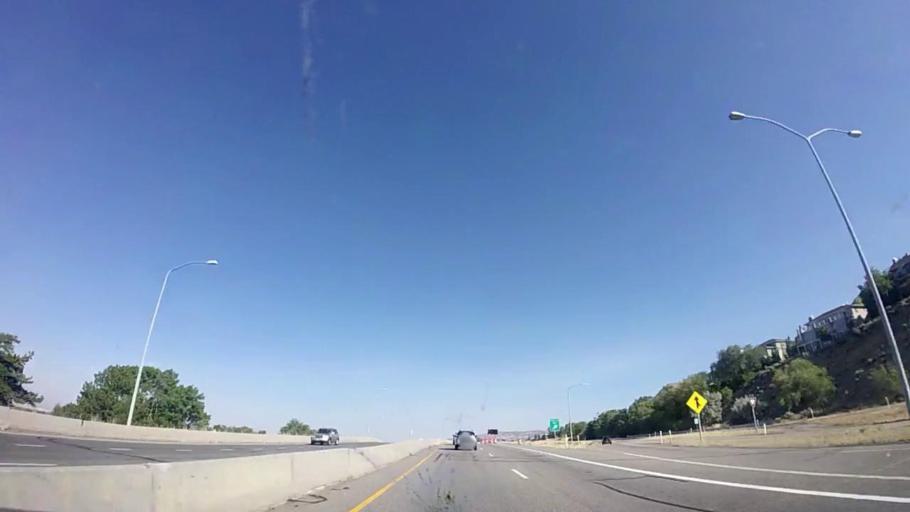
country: US
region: Utah
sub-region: Salt Lake County
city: East Millcreek
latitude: 40.7152
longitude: -111.8072
